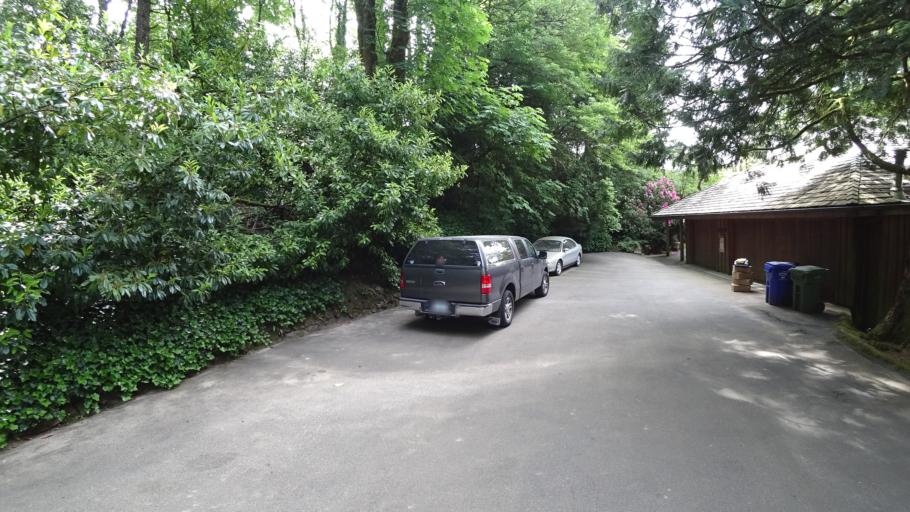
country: US
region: Oregon
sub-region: Clackamas County
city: Lake Oswego
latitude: 45.4418
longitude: -122.6690
